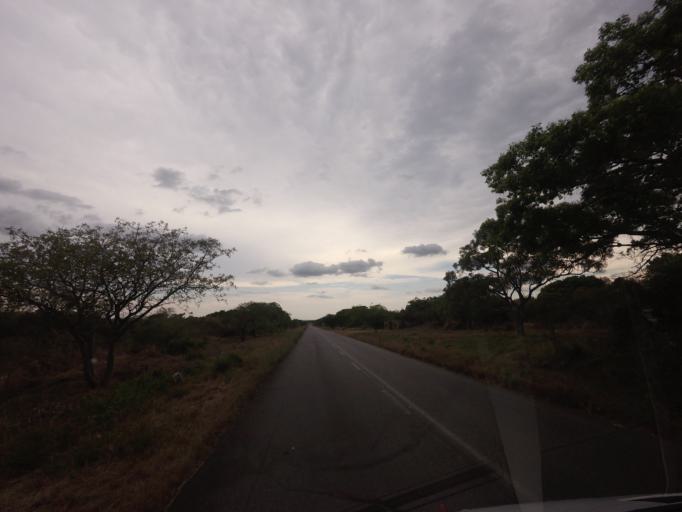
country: ZA
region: Limpopo
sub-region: Mopani District Municipality
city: Hoedspruit
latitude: -24.5073
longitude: 30.9159
